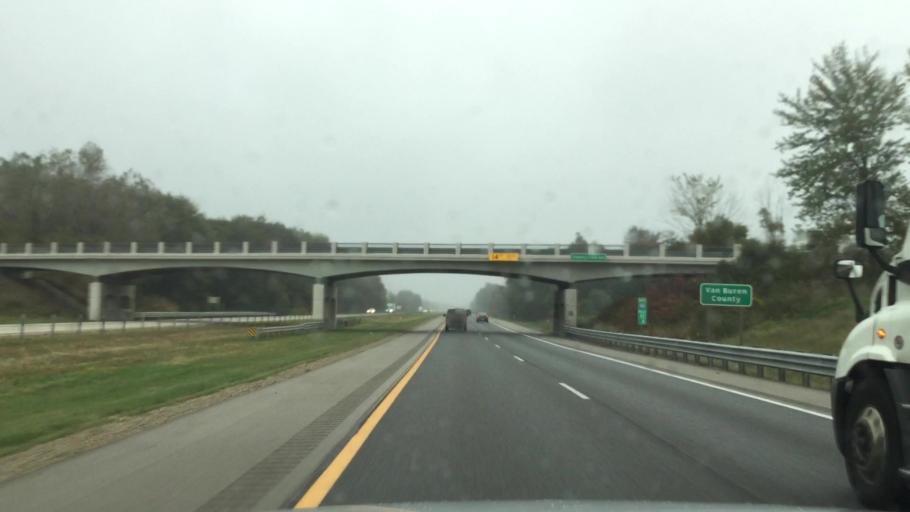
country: US
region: Michigan
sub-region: Berrien County
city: Watervliet
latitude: 42.1833
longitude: -86.2239
